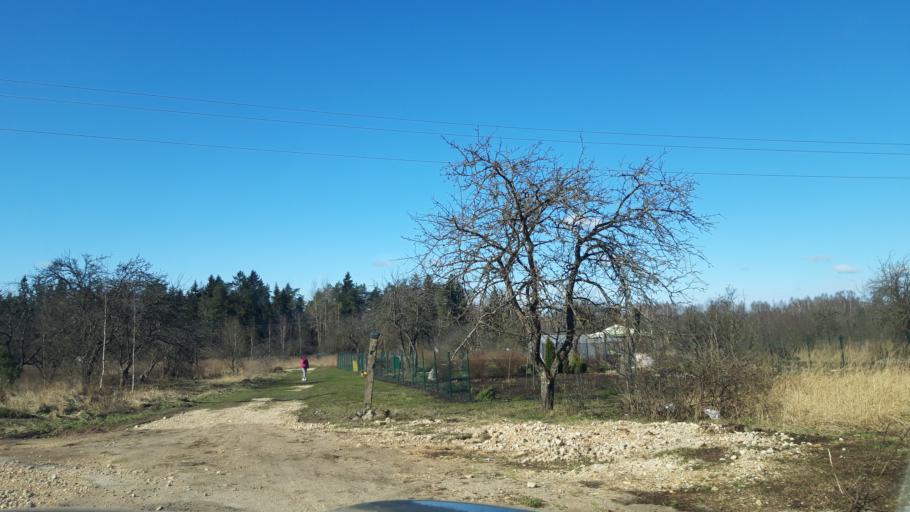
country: LV
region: Strenci
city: Seda
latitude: 57.6528
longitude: 25.7498
